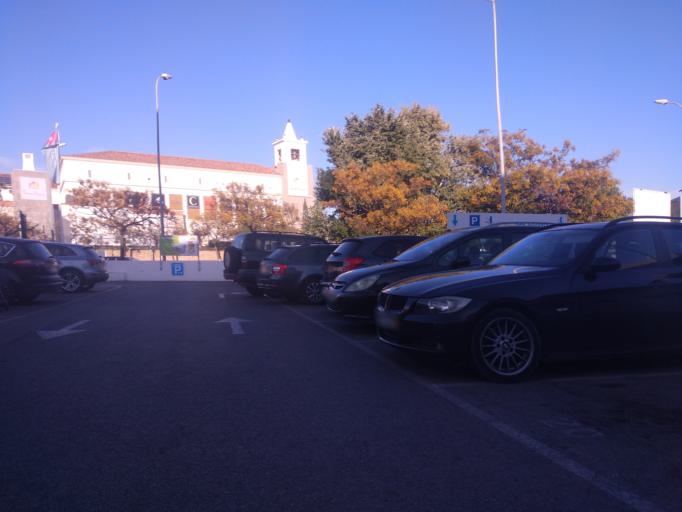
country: PT
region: Faro
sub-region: Faro
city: Faro
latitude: 37.0276
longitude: -7.9466
